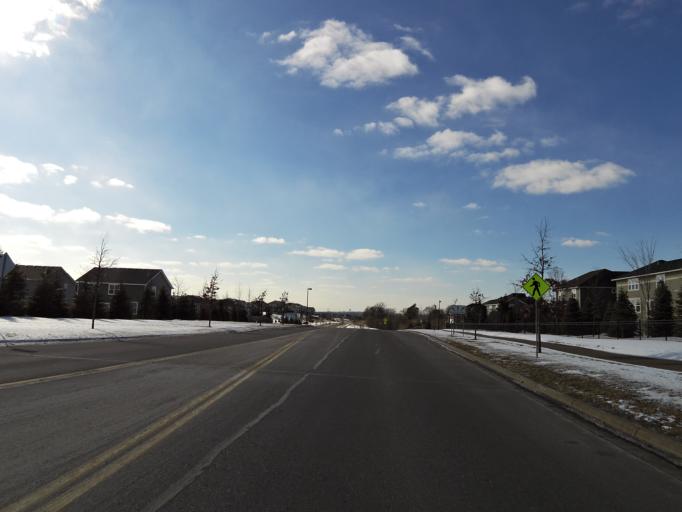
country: US
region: Minnesota
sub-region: Washington County
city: Woodbury
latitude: 44.9018
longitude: -92.8784
